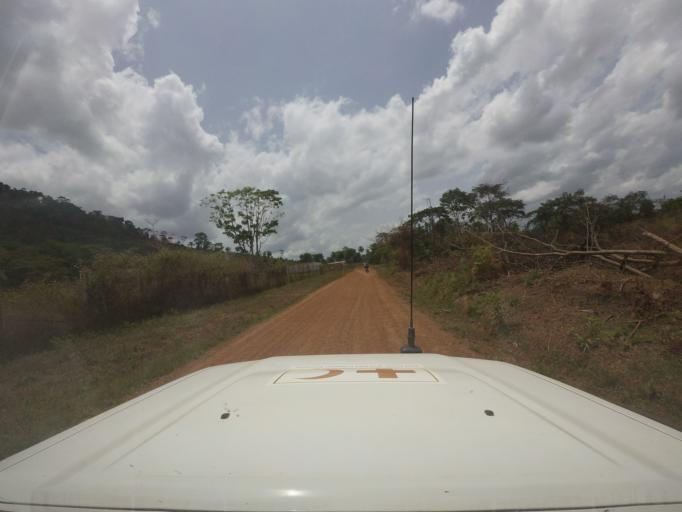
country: GN
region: Nzerekore
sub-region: Yomou
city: Yomou
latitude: 7.2442
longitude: -9.1760
